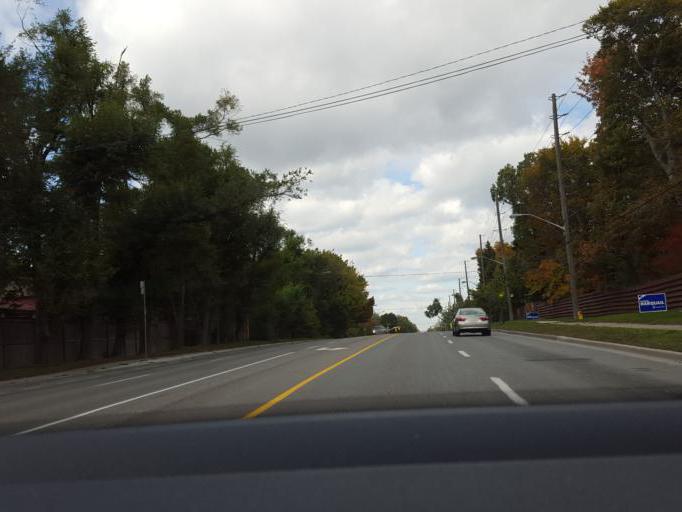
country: CA
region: Ontario
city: Willowdale
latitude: 43.7385
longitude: -79.3568
